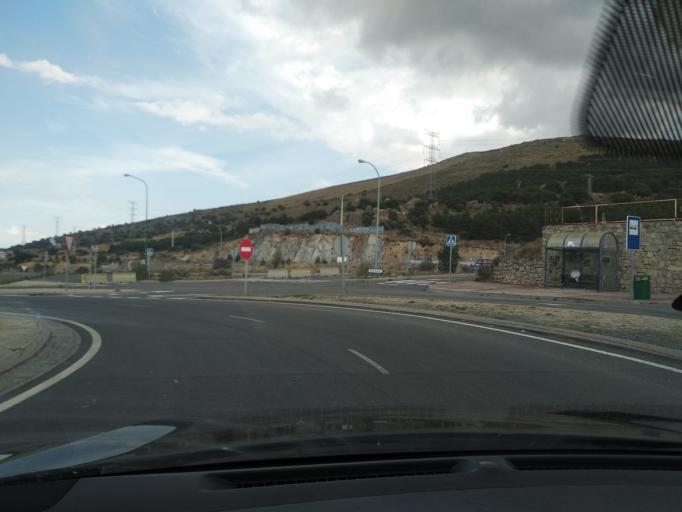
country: ES
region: Castille and Leon
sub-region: Provincia de Segovia
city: Otero de Herreros
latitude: 40.7770
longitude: -4.2087
